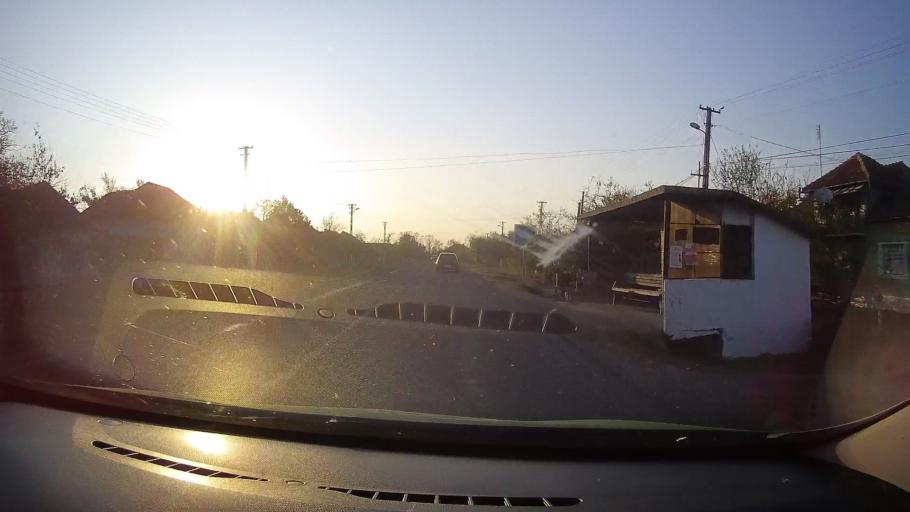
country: RO
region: Arad
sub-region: Comuna Bocsig
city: Bocsig
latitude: 46.4161
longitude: 21.9866
